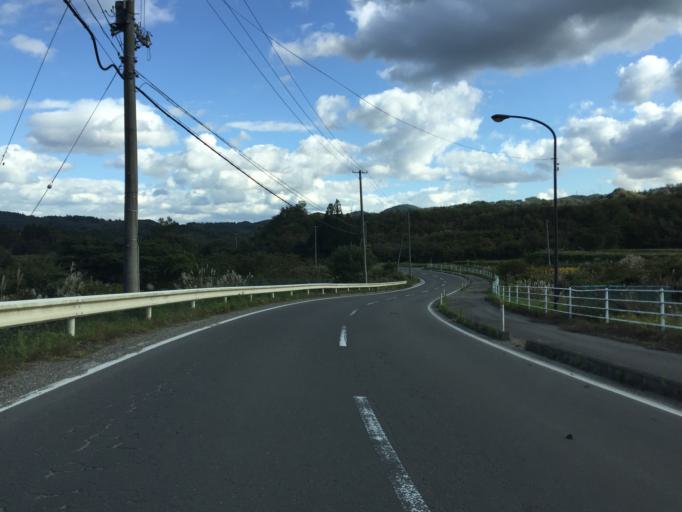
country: JP
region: Miyagi
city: Marumori
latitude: 37.8330
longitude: 140.8277
